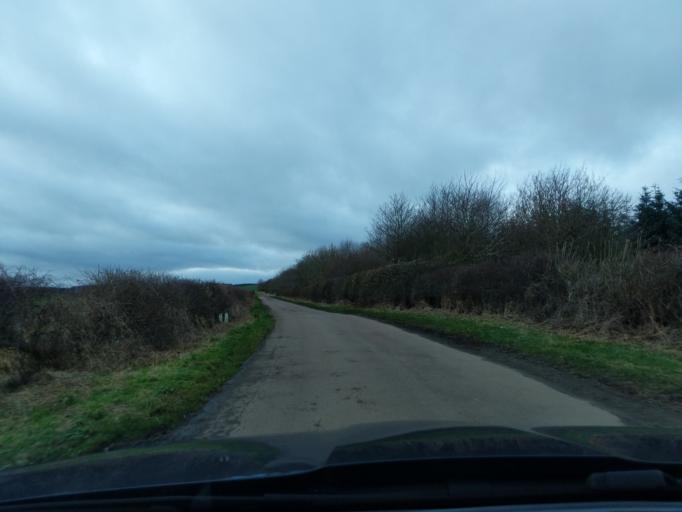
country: GB
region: England
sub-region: Northumberland
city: Ancroft
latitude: 55.7026
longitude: -2.0215
